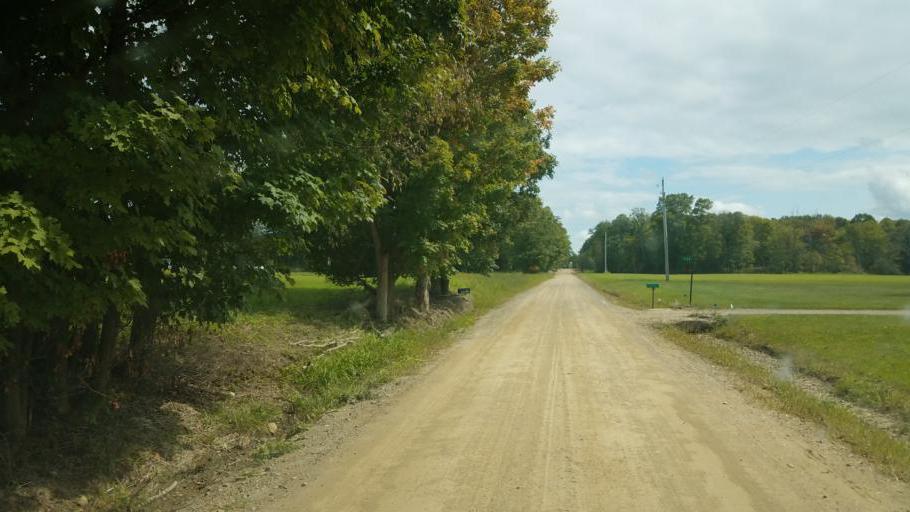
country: US
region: Pennsylvania
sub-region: Mercer County
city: Greenville
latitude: 41.4842
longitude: -80.3254
